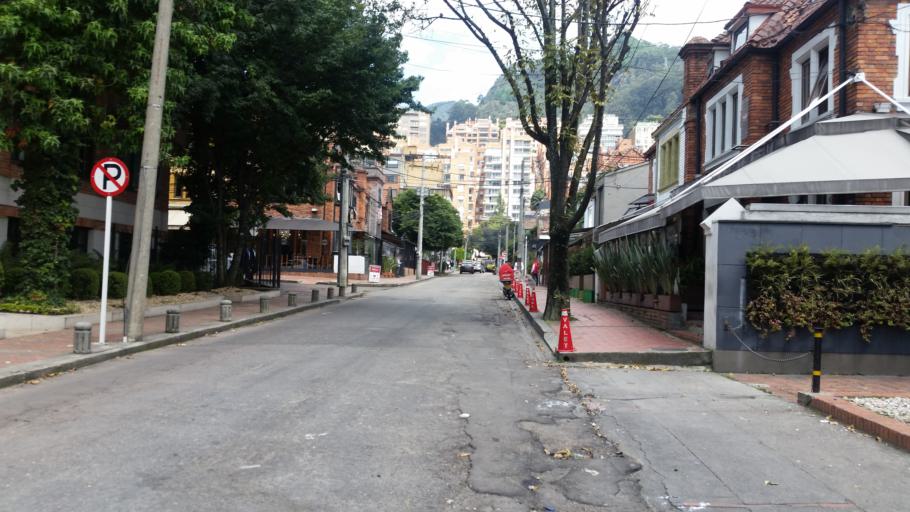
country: CO
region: Bogota D.C.
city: Barrio San Luis
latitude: 4.6516
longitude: -74.0559
